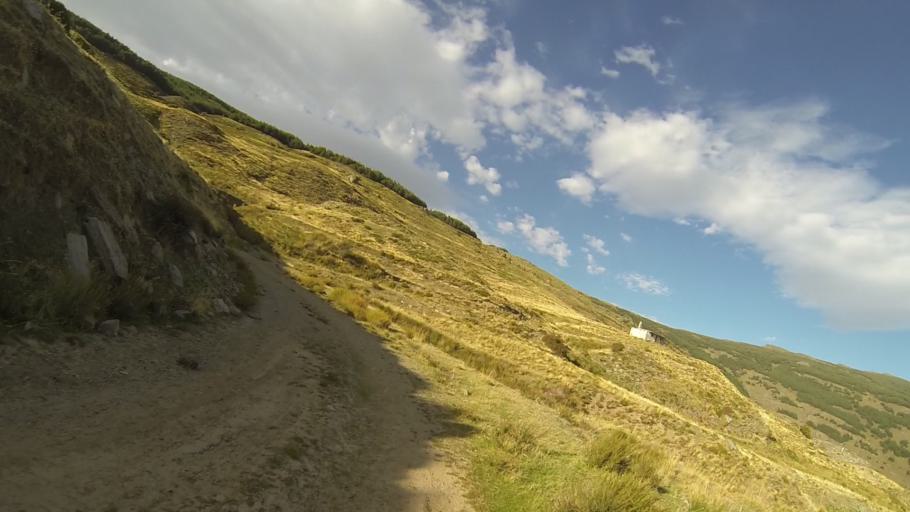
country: ES
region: Andalusia
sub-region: Provincia de Almeria
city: Laujar de Andarax
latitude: 37.0756
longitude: -2.8875
